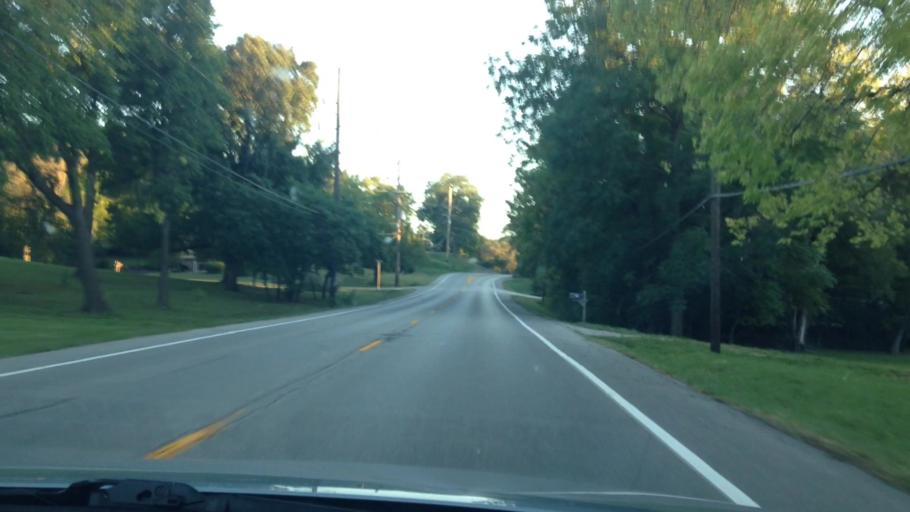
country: US
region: Missouri
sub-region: Platte County
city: Weatherby Lake
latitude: 39.2284
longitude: -94.6590
